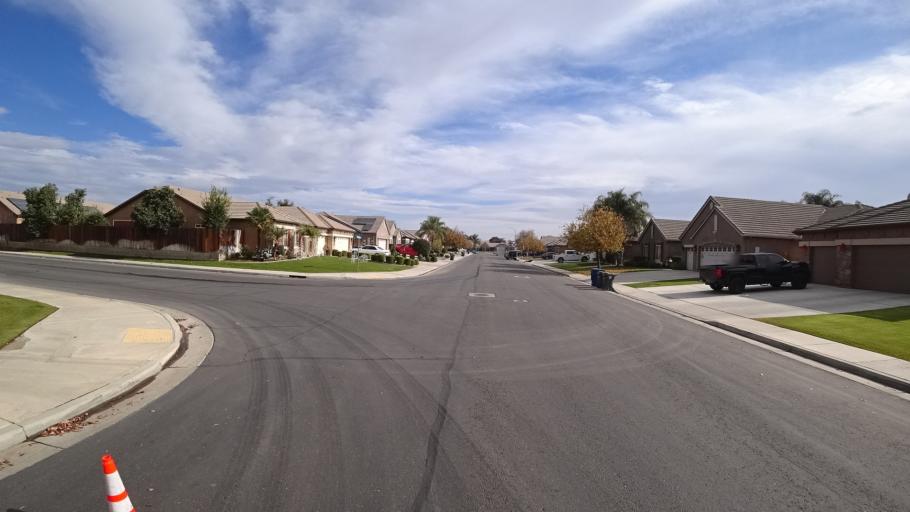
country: US
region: California
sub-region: Kern County
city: Rosedale
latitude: 35.4228
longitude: -119.1436
